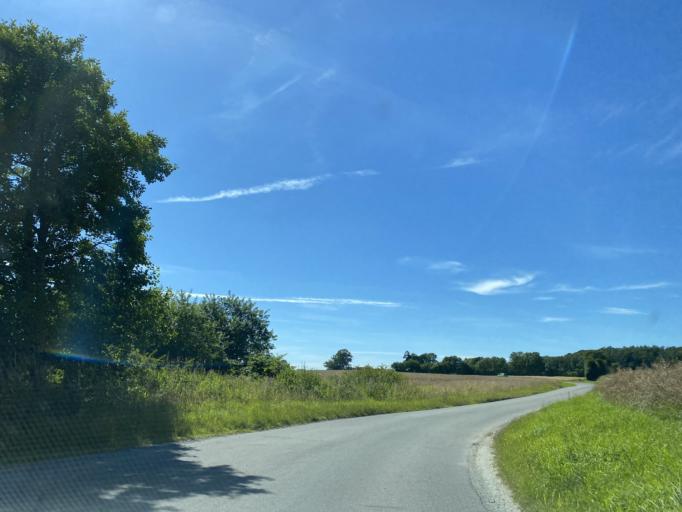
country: DK
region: South Denmark
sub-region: Kolding Kommune
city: Christiansfeld
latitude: 55.3885
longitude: 9.5207
